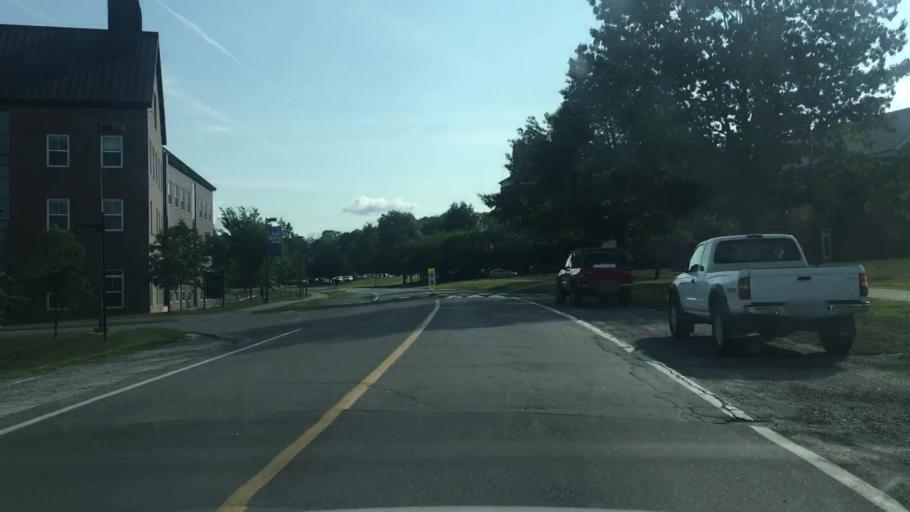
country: US
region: Maine
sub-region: Kennebec County
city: Waterville
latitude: 44.5654
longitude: -69.6594
